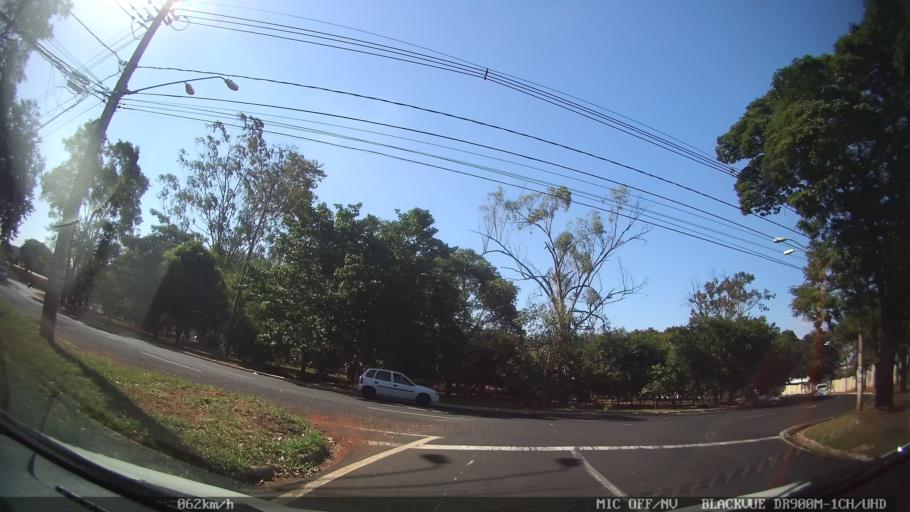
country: BR
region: Sao Paulo
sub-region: Ribeirao Preto
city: Ribeirao Preto
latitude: -21.1940
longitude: -47.7615
